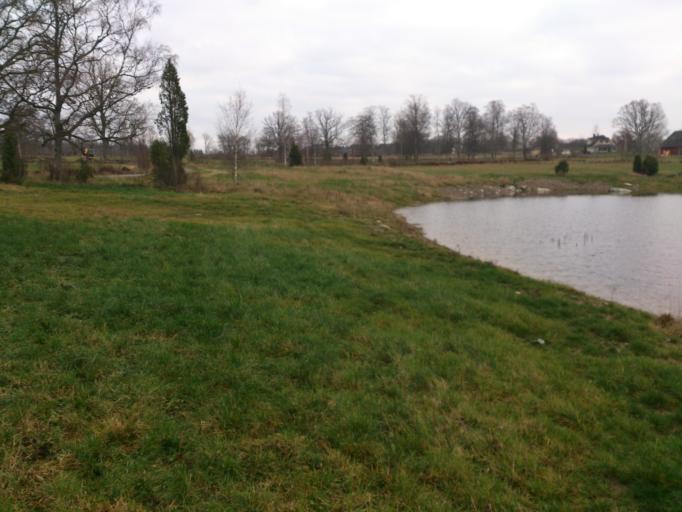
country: SE
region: Joenkoeping
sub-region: Vetlanda Kommun
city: Vetlanda
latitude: 57.4659
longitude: 15.0605
